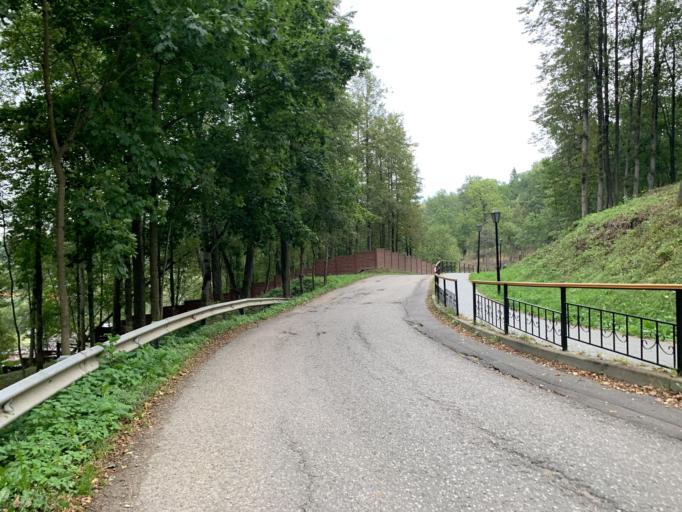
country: RU
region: Moskovskaya
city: Zvenigorod
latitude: 55.7333
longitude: 36.8099
